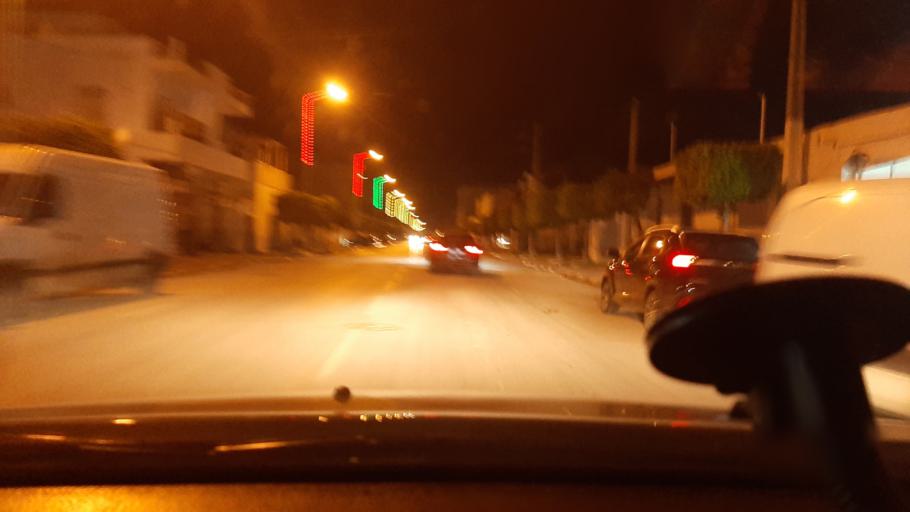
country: TN
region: Safaqis
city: Sfax
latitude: 34.7784
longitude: 10.7258
